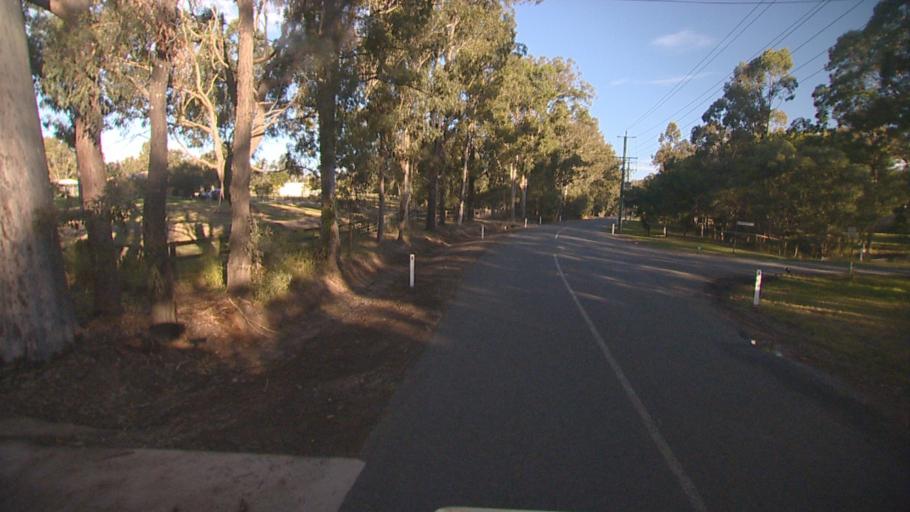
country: AU
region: Queensland
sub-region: Logan
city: Waterford West
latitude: -27.7371
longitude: 153.1454
